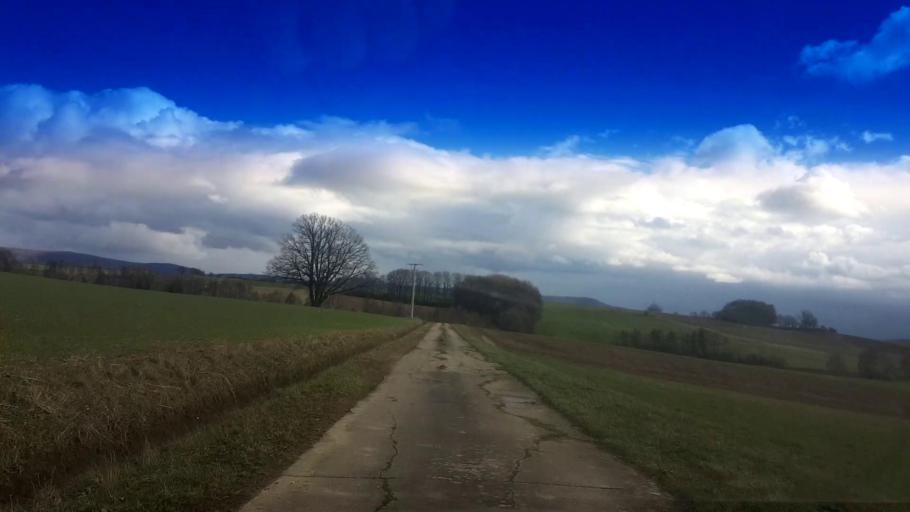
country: DE
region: Bavaria
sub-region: Upper Franconia
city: Schesslitz
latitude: 49.9924
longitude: 11.0171
